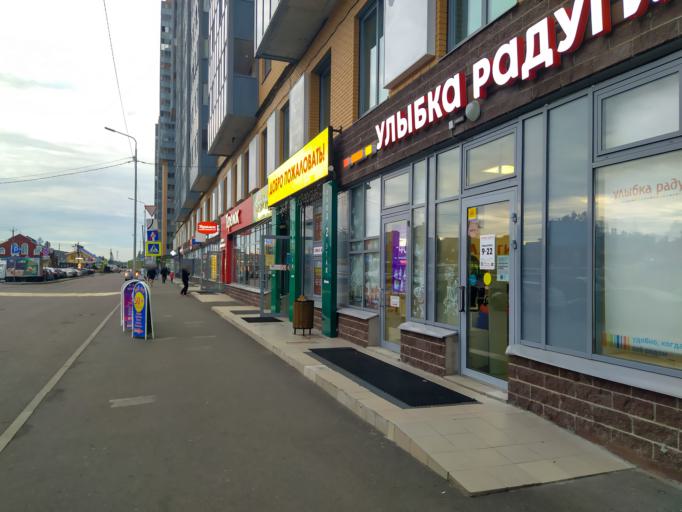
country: RU
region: Leningrad
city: Murino
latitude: 60.0498
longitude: 30.4447
